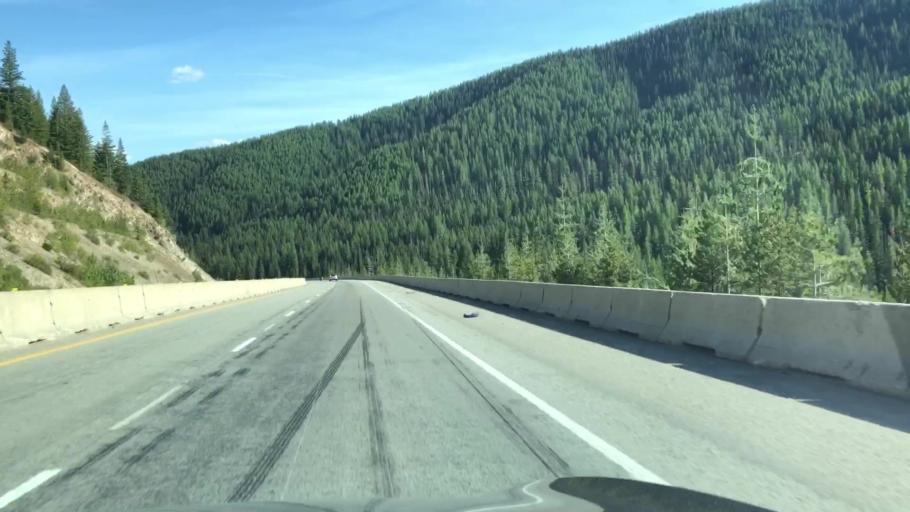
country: US
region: Idaho
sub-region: Shoshone County
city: Wallace
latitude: 47.4392
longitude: -115.6837
